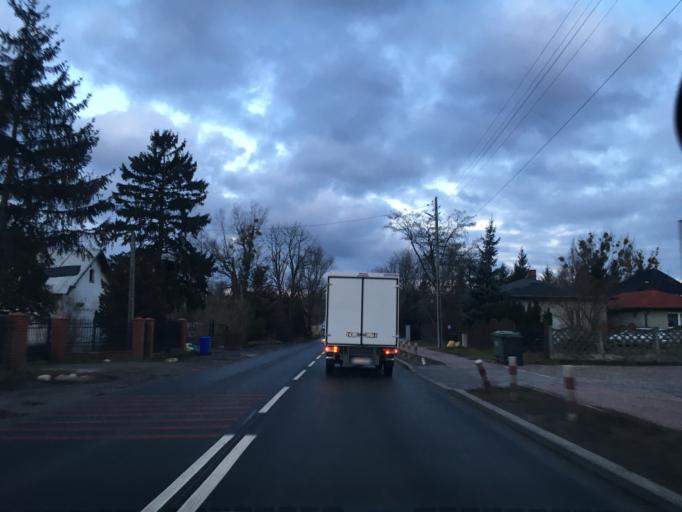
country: PL
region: Masovian Voivodeship
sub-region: Powiat grodziski
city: Milanowek
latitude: 52.0883
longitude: 20.6782
